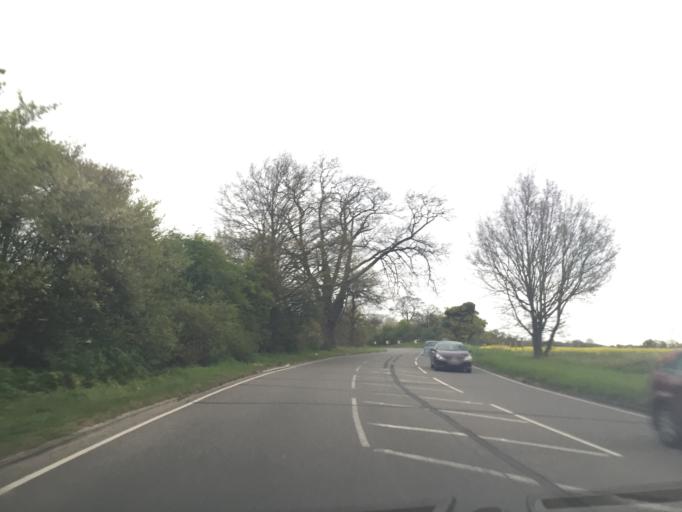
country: GB
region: England
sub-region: Essex
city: Theydon Bois
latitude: 51.6619
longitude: 0.1143
